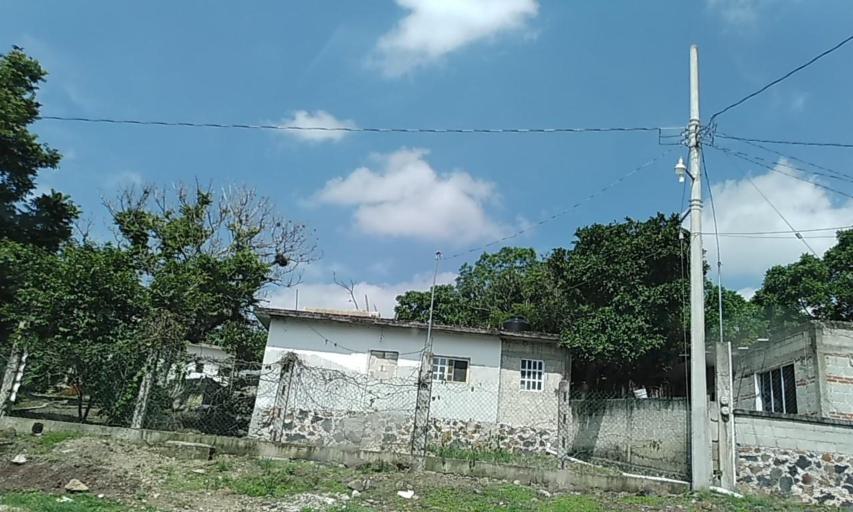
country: MX
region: Veracruz
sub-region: Emiliano Zapata
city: Dos Rios
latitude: 19.4446
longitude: -96.7837
